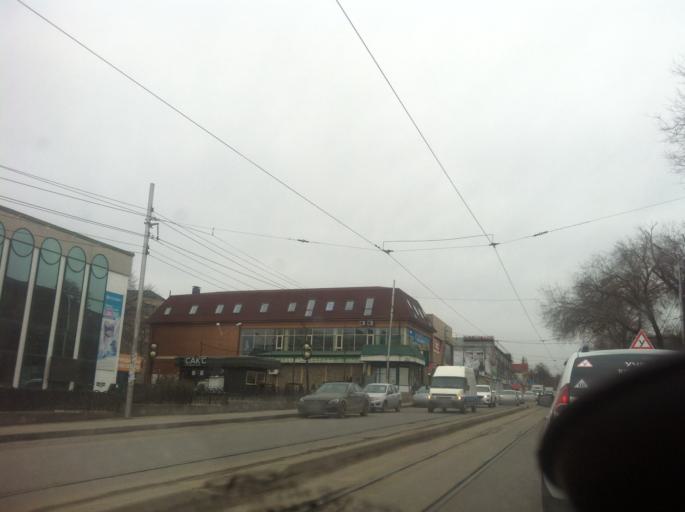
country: RU
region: Stavropol'skiy
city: Pyatigorsk
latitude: 44.0404
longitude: 43.0644
